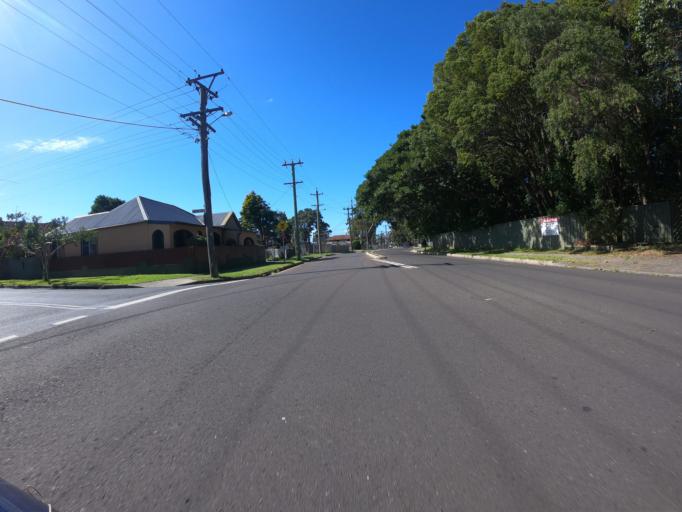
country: AU
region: New South Wales
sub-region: Wollongong
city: Corrimal
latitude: -34.3739
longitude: 150.9043
